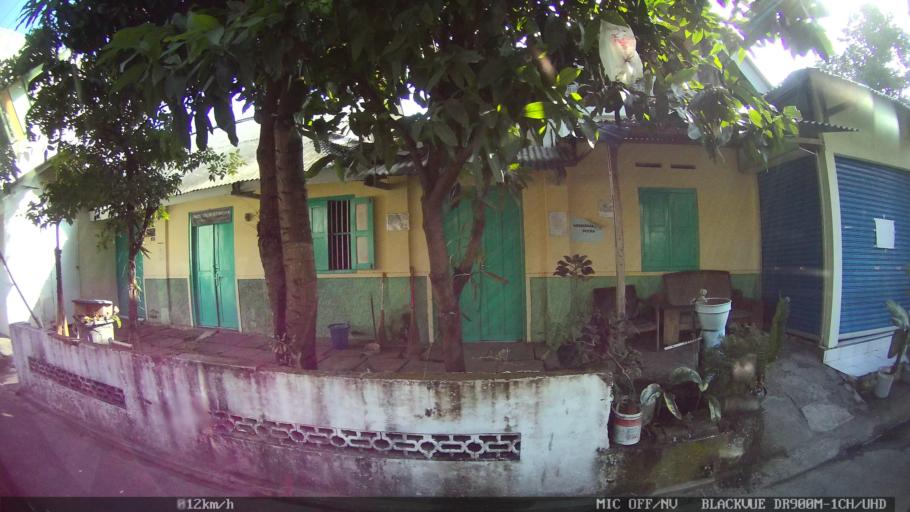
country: ID
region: Daerah Istimewa Yogyakarta
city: Yogyakarta
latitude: -7.7722
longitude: 110.3907
